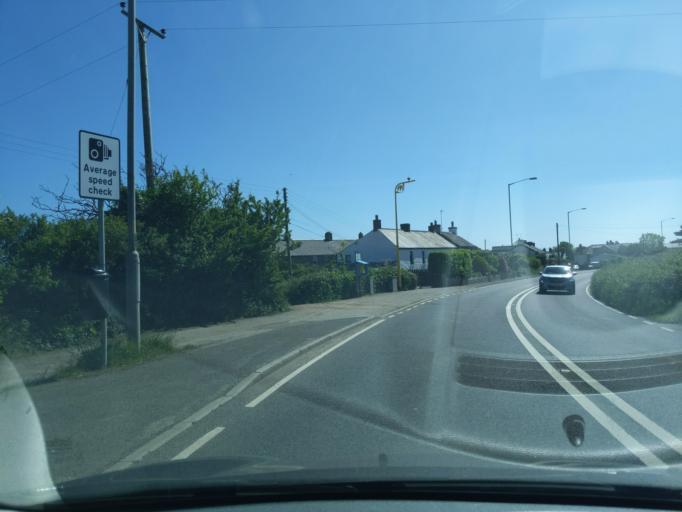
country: GB
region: England
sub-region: Cornwall
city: Wendron
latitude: 50.1135
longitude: -5.2462
